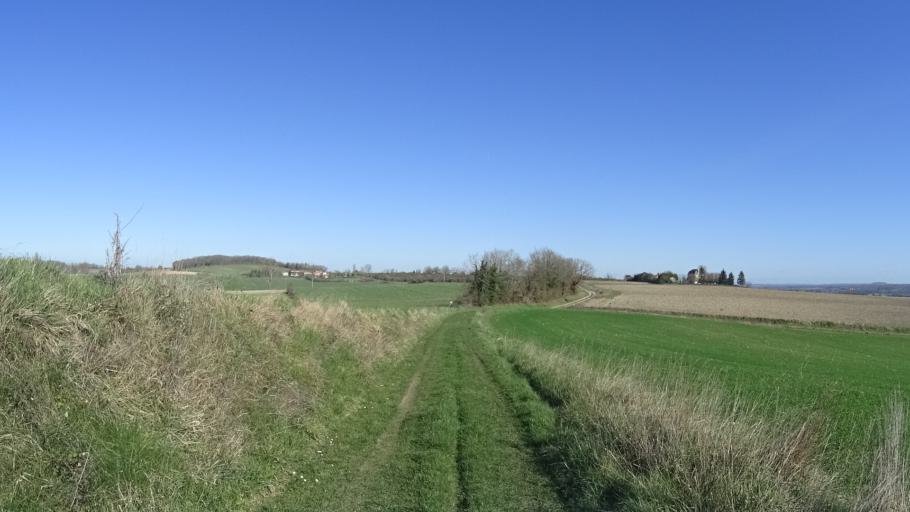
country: FR
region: Aquitaine
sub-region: Departement de la Dordogne
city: Saint-Aulaye
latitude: 45.2352
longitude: 0.1321
